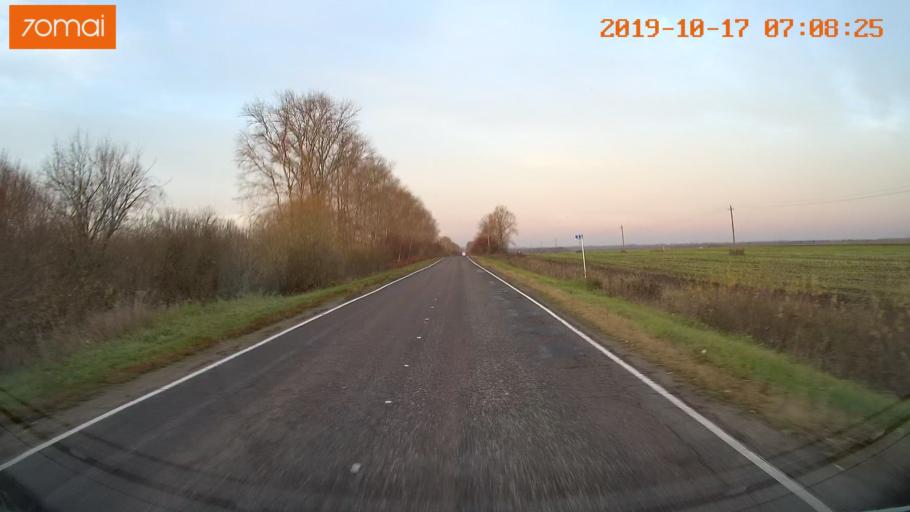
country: RU
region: Vladimir
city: Suzdal'
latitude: 56.4223
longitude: 40.4069
